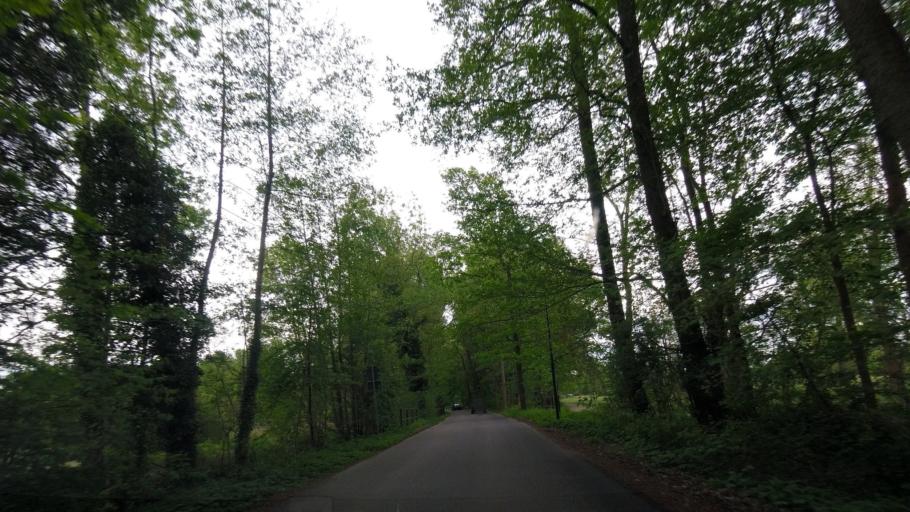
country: DE
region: Brandenburg
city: Lubbenau
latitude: 51.8687
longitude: 13.9838
